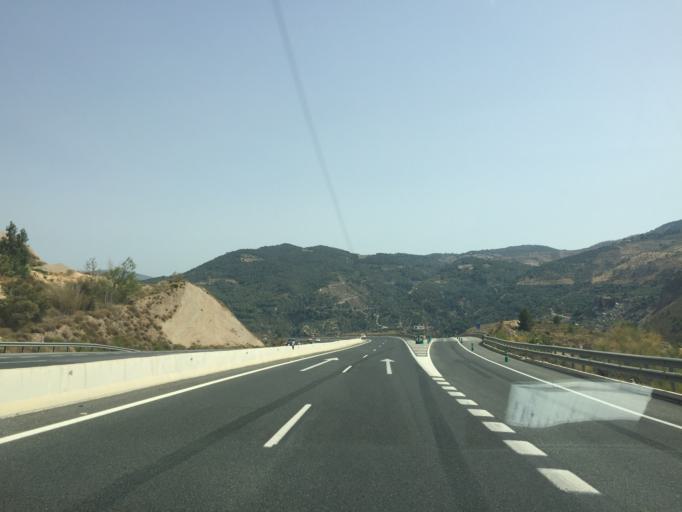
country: ES
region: Andalusia
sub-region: Provincia de Granada
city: Lanjaron
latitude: 36.9051
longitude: -3.5264
